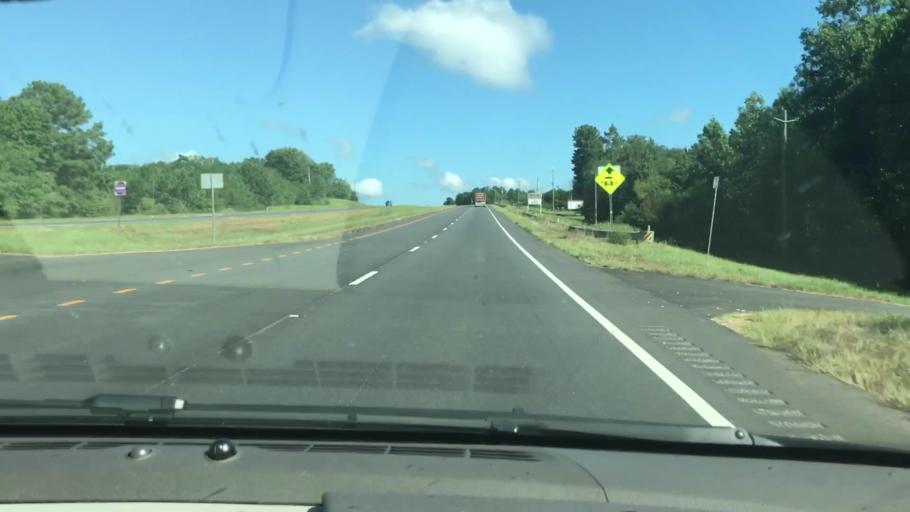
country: US
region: Alabama
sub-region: Barbour County
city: Eufaula
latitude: 32.0251
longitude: -85.1195
